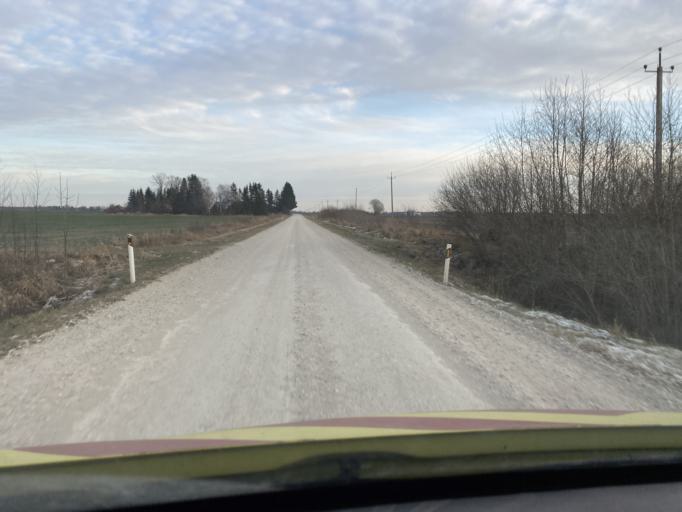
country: EE
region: Jogevamaa
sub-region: Poltsamaa linn
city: Poltsamaa
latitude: 58.5825
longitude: 26.0609
